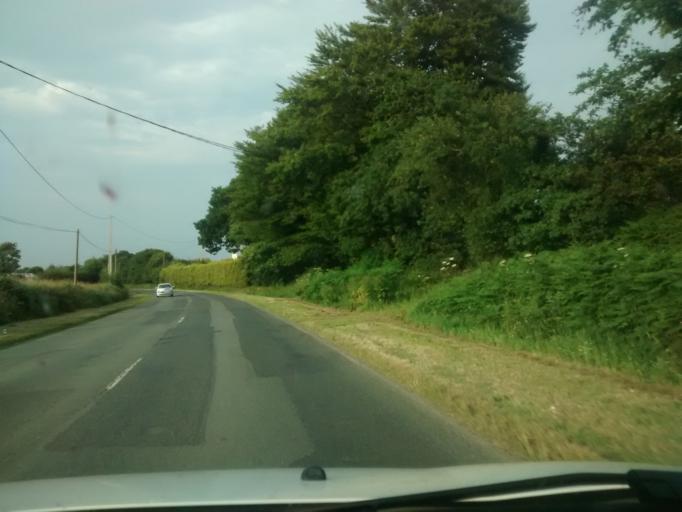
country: FR
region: Brittany
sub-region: Departement des Cotes-d'Armor
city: Saint-Quay-Perros
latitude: 48.7618
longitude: -3.4333
